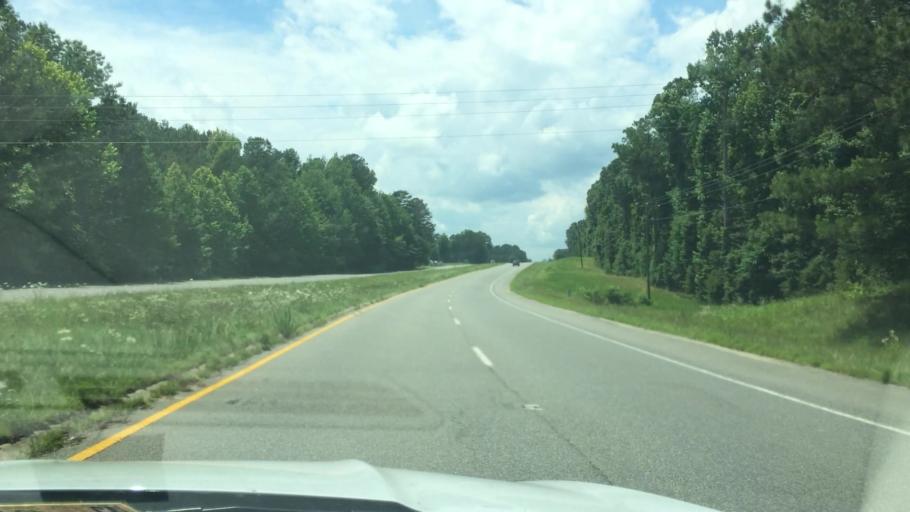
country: US
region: Virginia
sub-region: Middlesex County
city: Saluda
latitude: 37.5624
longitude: -76.6278
